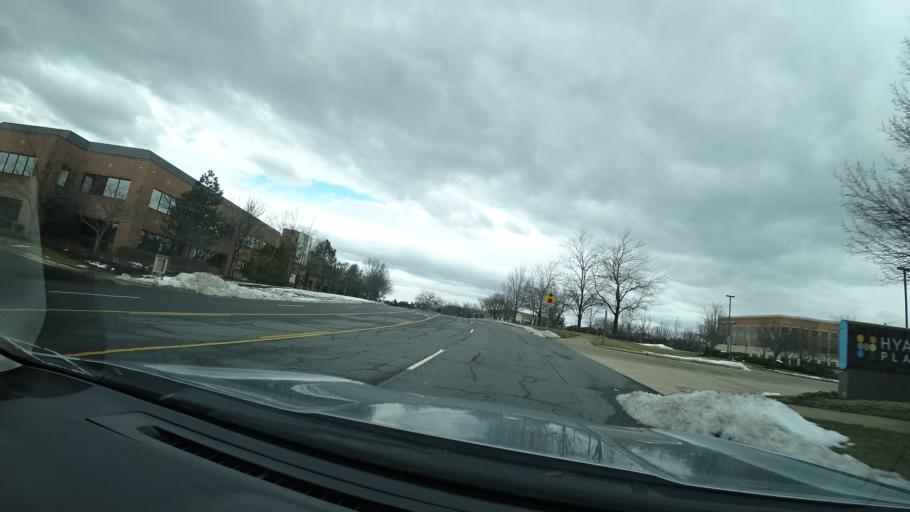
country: US
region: Virginia
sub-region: Loudoun County
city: Dulles Town Center
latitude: 39.0306
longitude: -77.4073
